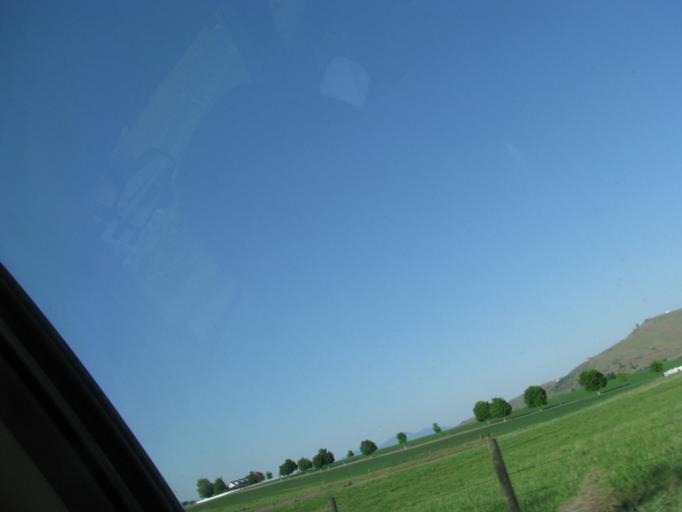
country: US
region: Washington
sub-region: Spokane County
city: Liberty Lake
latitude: 47.6341
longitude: -117.1536
